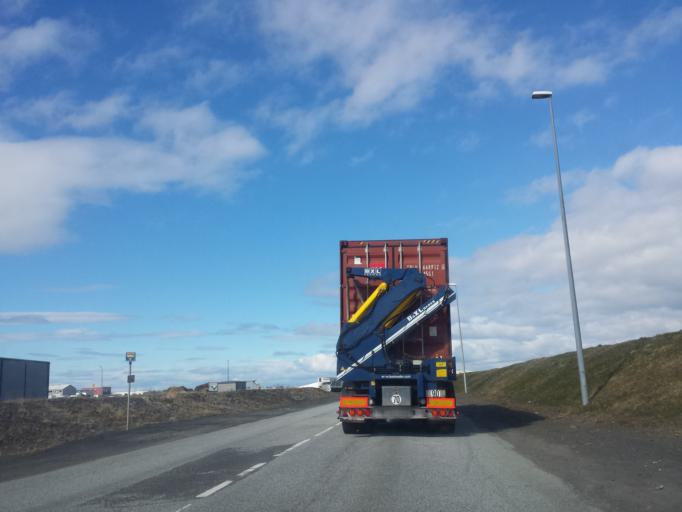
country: IS
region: Capital Region
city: Hafnarfjoerdur
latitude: 64.0760
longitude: -21.9283
